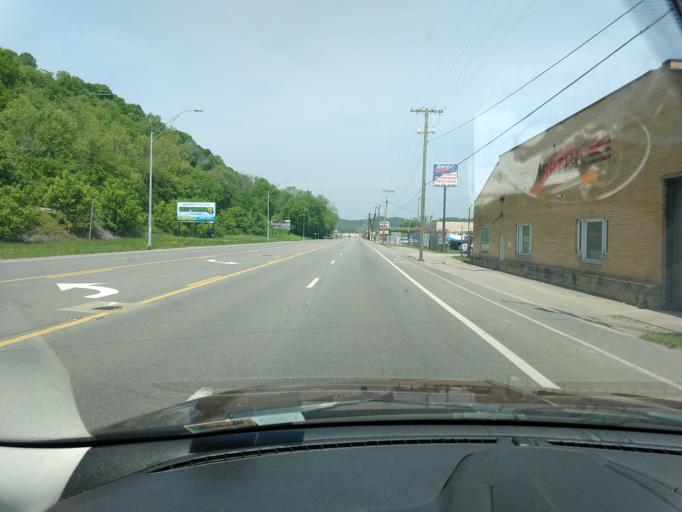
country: US
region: West Virginia
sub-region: Kanawha County
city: Dunbar
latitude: 38.3627
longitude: -81.7607
